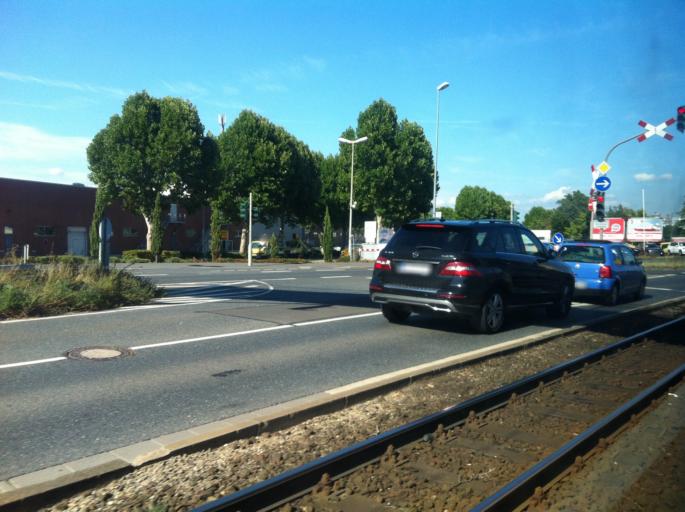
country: DE
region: Rheinland-Pfalz
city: Mainz
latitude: 50.0154
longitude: 8.2357
